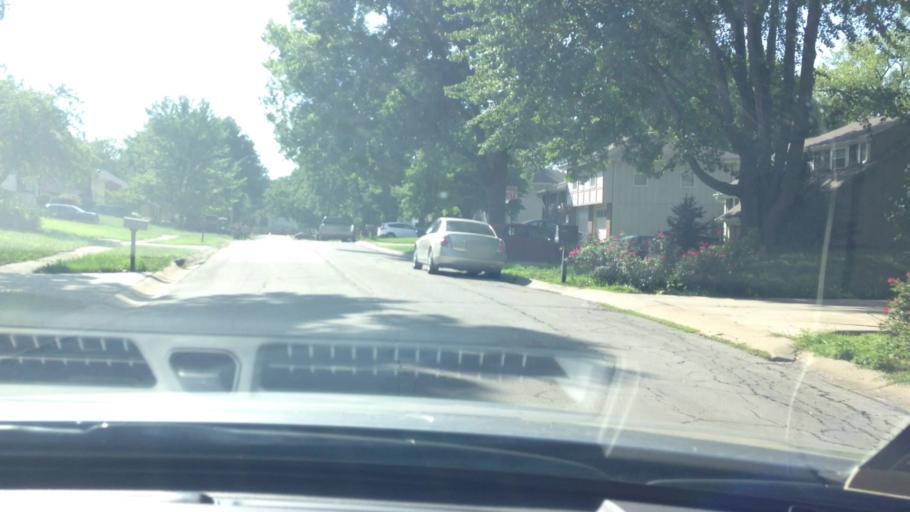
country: US
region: Missouri
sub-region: Jackson County
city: Grandview
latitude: 38.8828
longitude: -94.5047
